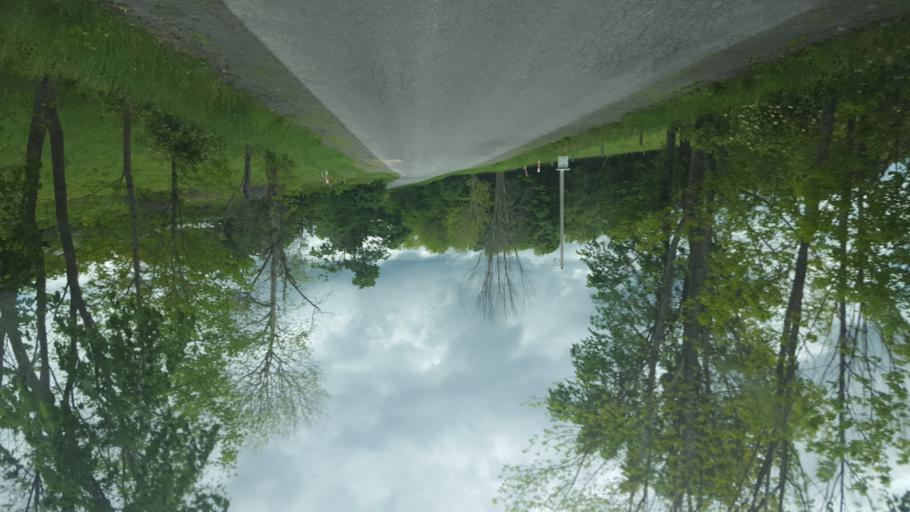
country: US
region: New York
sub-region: Otsego County
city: Richfield Springs
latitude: 42.8714
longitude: -75.0587
